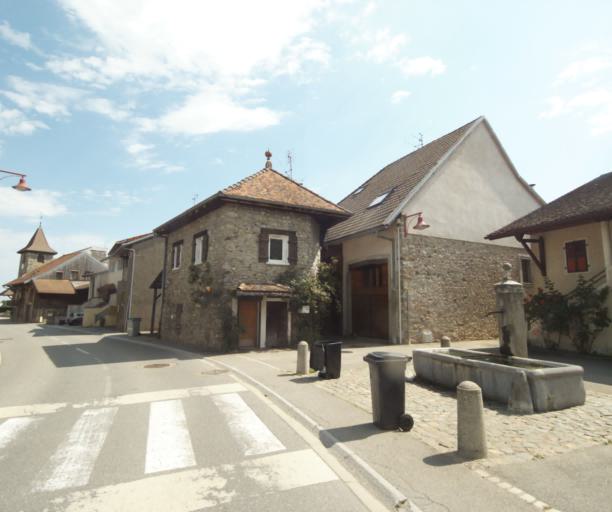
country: FR
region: Rhone-Alpes
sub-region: Departement de la Haute-Savoie
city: Armoy
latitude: 46.3493
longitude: 6.5211
